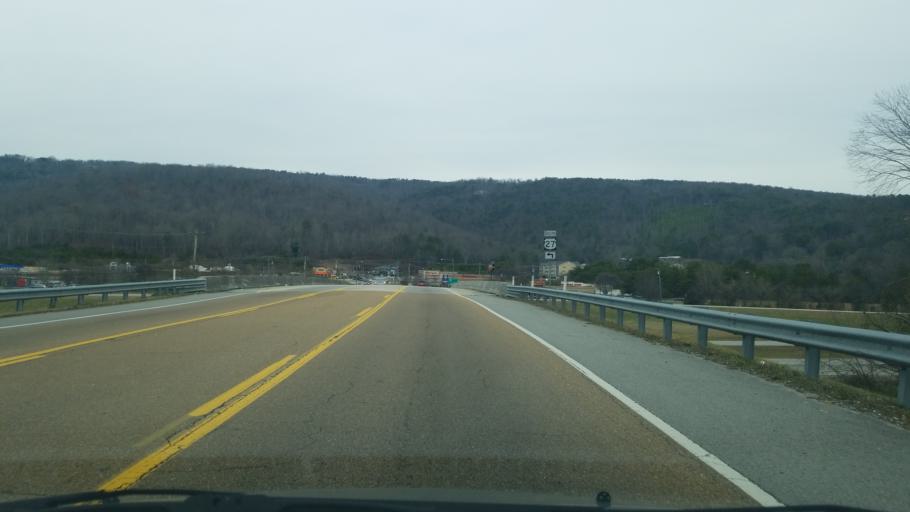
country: US
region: Tennessee
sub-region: Hamilton County
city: Soddy-Daisy
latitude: 35.2342
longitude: -85.1957
